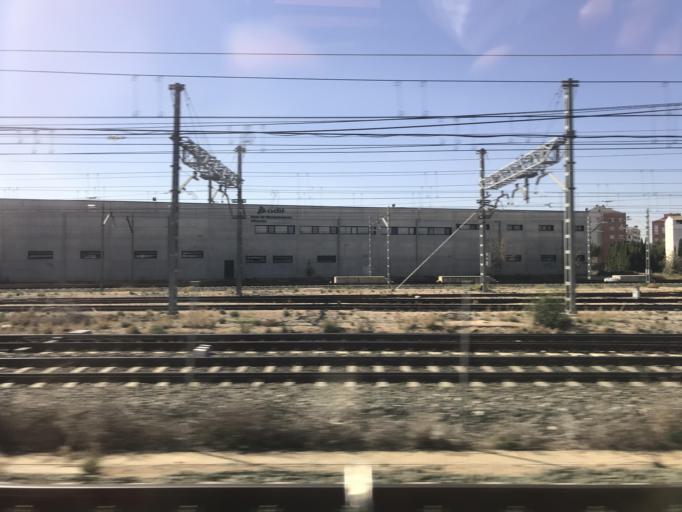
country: ES
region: Castille-La Mancha
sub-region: Provincia de Albacete
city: Albacete
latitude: 39.0050
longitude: -1.8522
